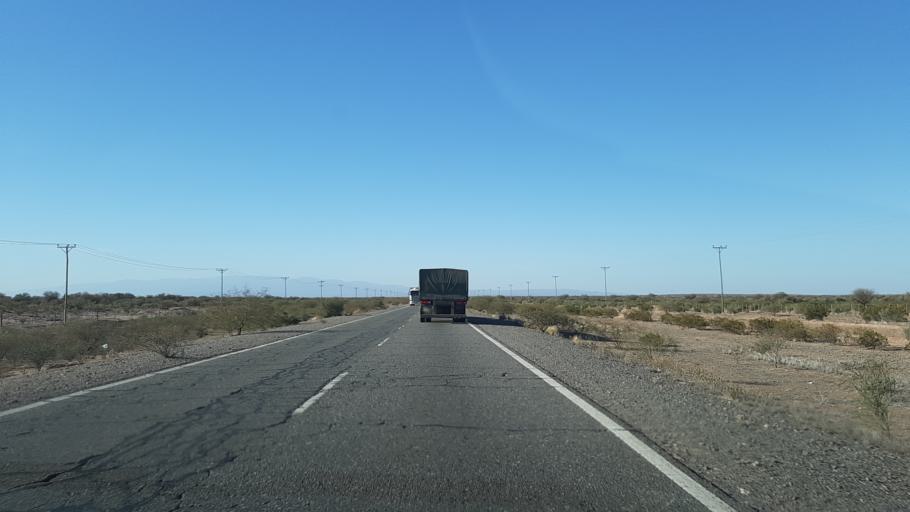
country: AR
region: San Juan
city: Caucete
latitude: -31.6532
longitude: -67.7679
